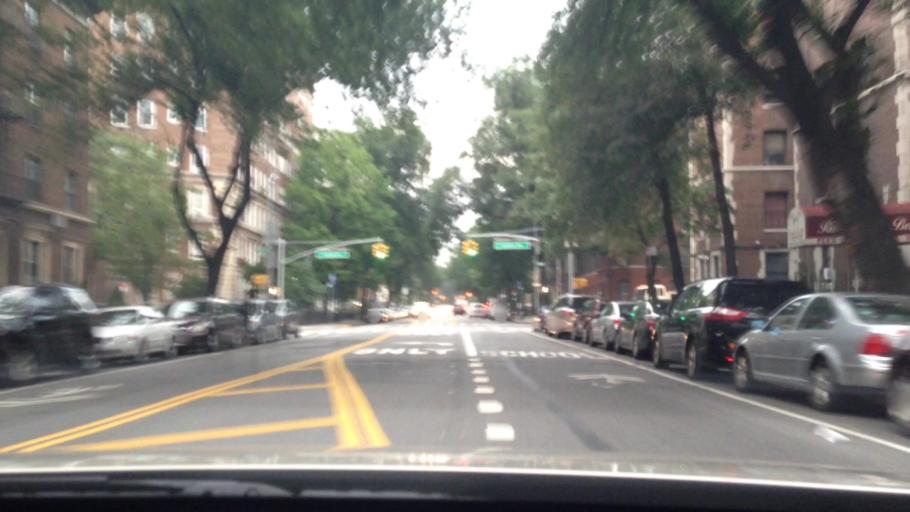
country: US
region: New York
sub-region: Kings County
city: Brooklyn
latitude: 40.6515
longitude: -73.9614
